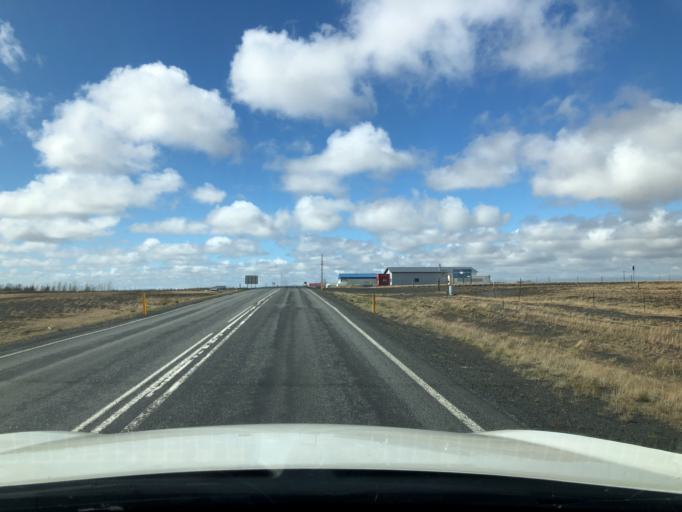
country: IS
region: South
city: Vestmannaeyjar
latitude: 63.8289
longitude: -20.3796
